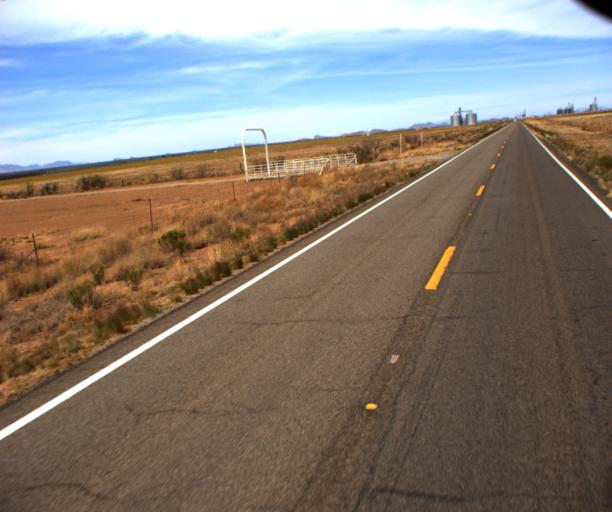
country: US
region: Arizona
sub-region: Cochise County
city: Tombstone
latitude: 31.7471
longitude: -109.6885
